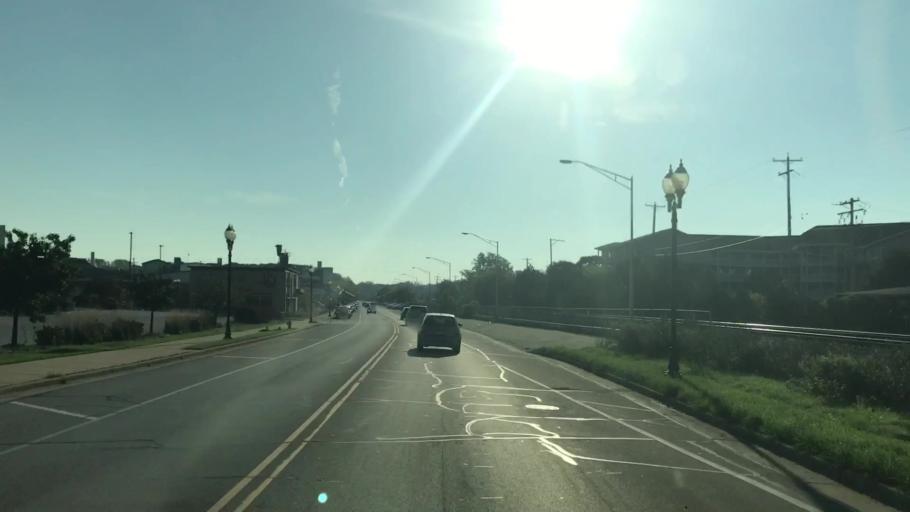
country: US
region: Wisconsin
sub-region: Milwaukee County
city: Wauwatosa
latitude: 43.0457
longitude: -87.9960
